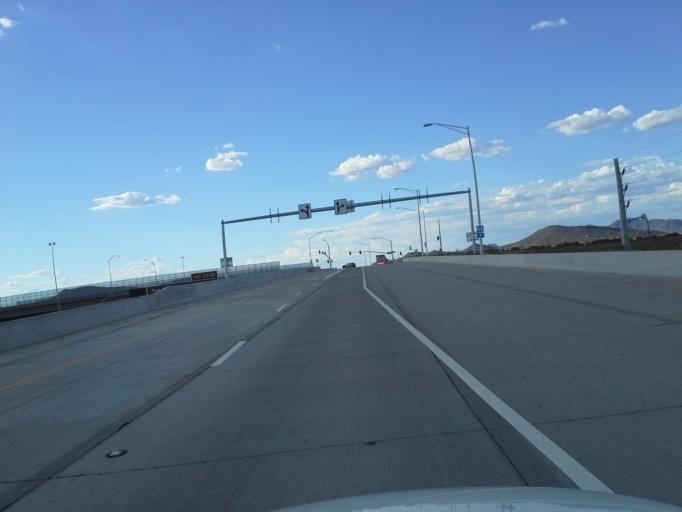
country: US
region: Arizona
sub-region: Maricopa County
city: Anthem
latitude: 33.7817
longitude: -112.1312
